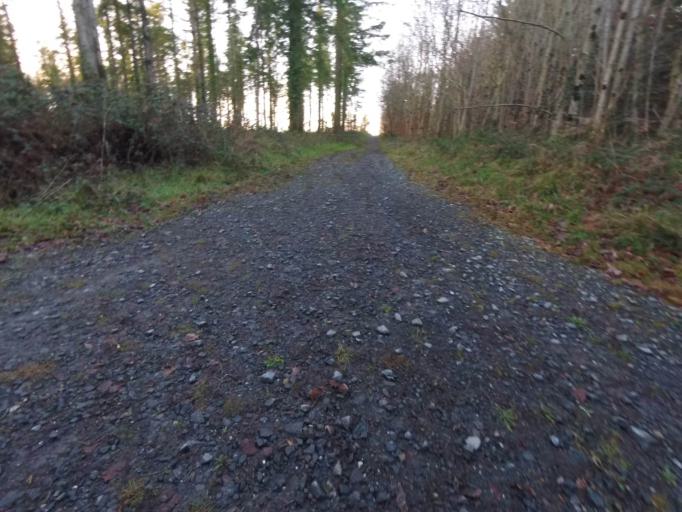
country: IE
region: Munster
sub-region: Waterford
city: Portlaw
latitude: 52.3035
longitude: -7.3420
